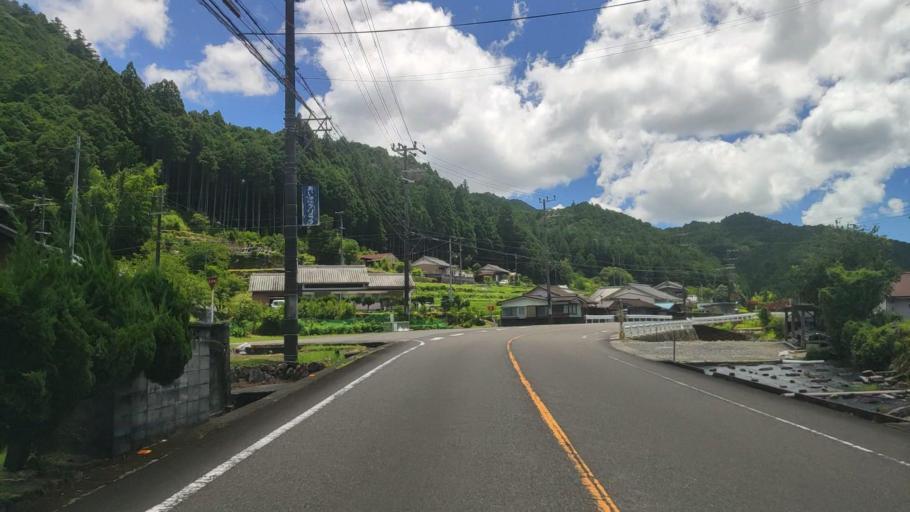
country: JP
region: Mie
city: Owase
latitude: 33.9740
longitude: 136.0582
